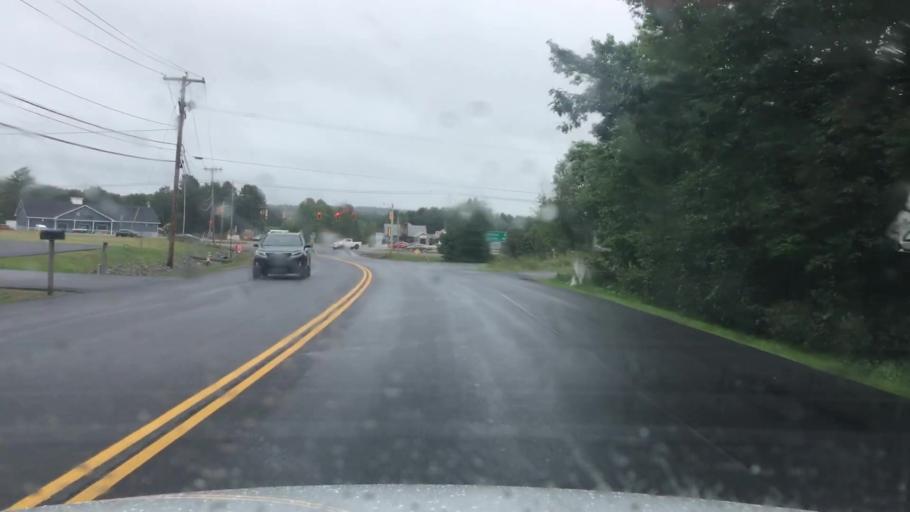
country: US
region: Maine
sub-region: Penobscot County
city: Hampden
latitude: 44.7552
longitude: -68.8412
